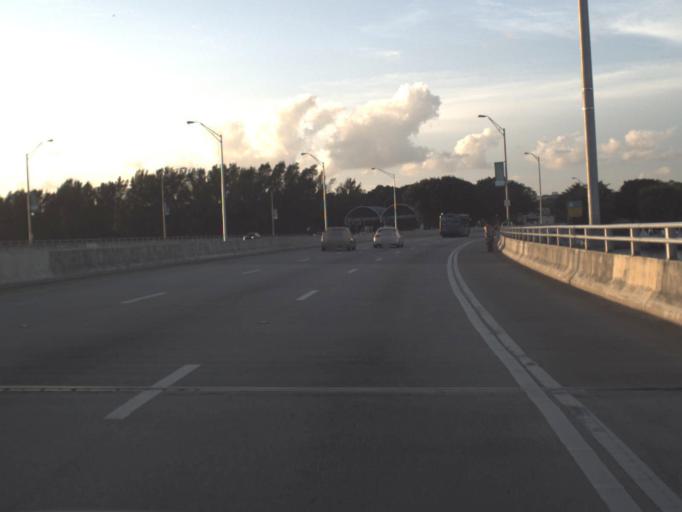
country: US
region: Florida
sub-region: Miami-Dade County
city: Miami
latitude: 25.7472
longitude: -80.2003
